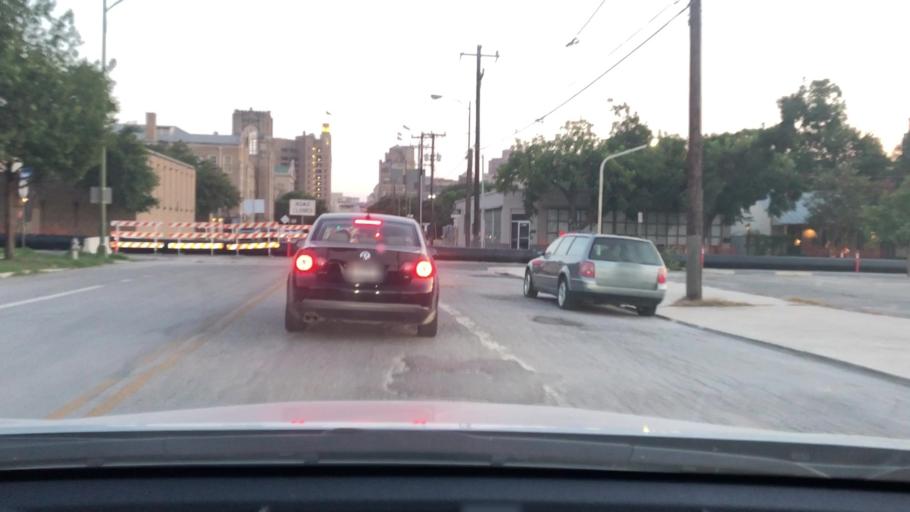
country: US
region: Texas
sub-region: Bexar County
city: San Antonio
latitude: 29.4299
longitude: -98.4823
